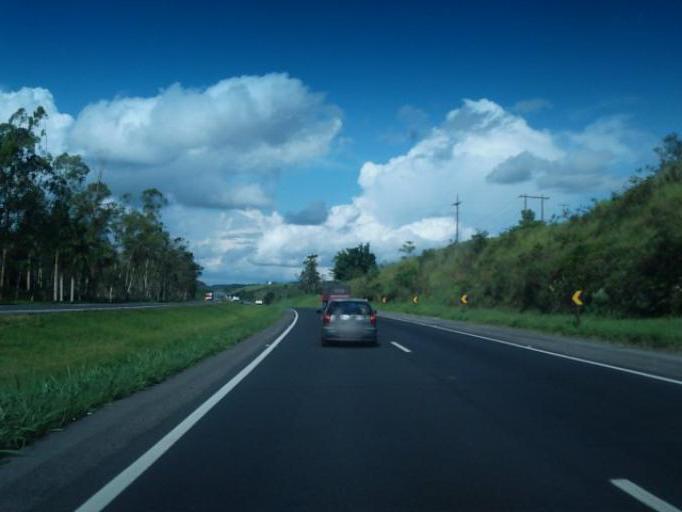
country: BR
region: Sao Paulo
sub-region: Registro
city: Registro
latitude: -24.4188
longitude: -47.7658
